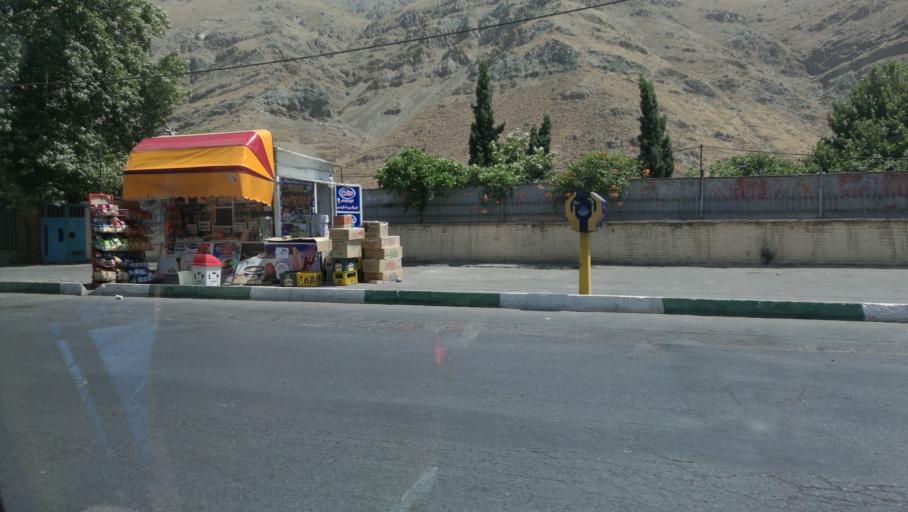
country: IR
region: Alborz
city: Karaj
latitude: 35.8353
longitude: 51.0461
